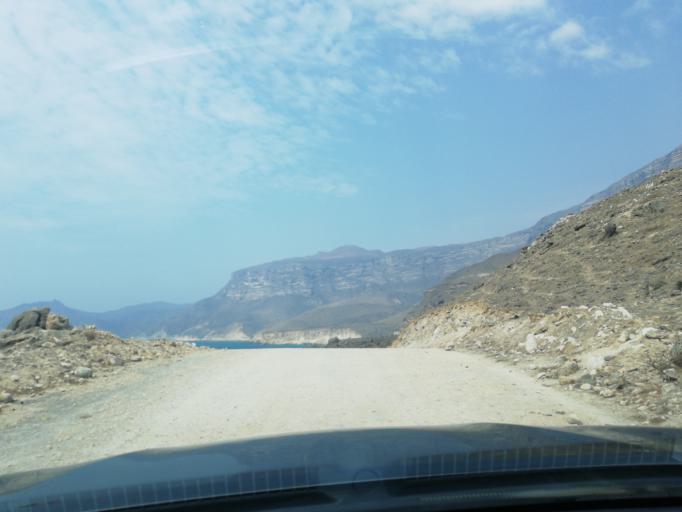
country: OM
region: Zufar
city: Salalah
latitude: 16.8195
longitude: 53.6953
